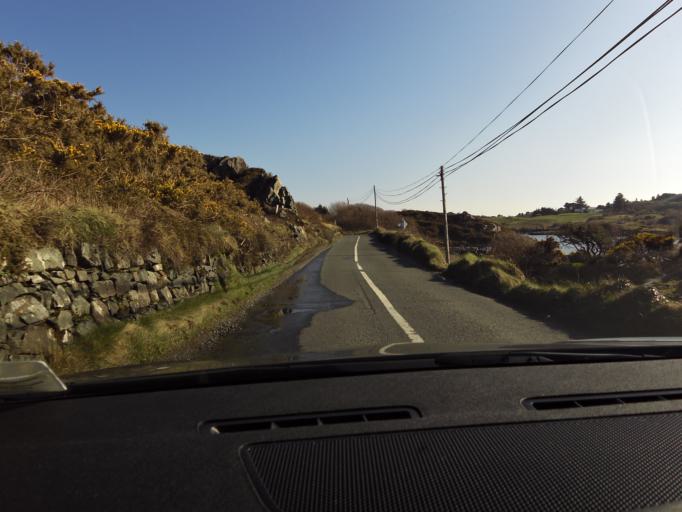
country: IE
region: Connaught
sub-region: County Galway
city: Clifden
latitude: 53.4707
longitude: -10.0192
